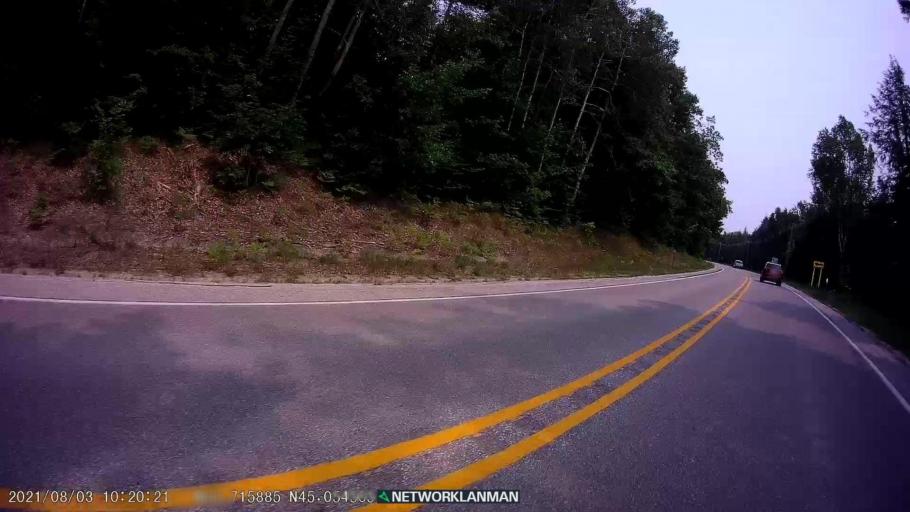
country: US
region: Michigan
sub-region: Leelanau County
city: Leland
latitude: 45.0546
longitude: -85.7158
